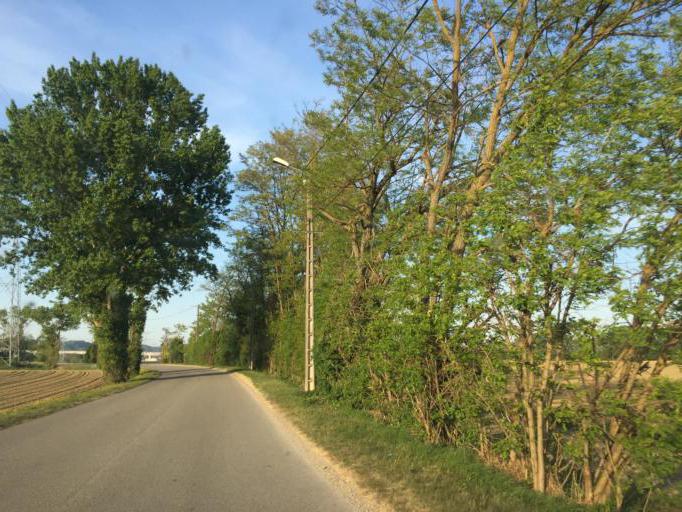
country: FR
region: Rhone-Alpes
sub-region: Departement de l'Ain
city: Beynost
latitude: 45.8209
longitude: 4.9996
